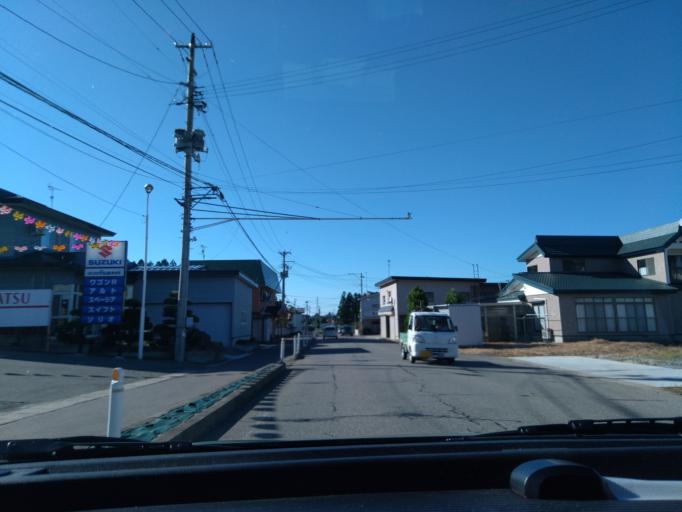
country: JP
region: Akita
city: Yokotemachi
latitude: 39.2823
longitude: 140.5579
